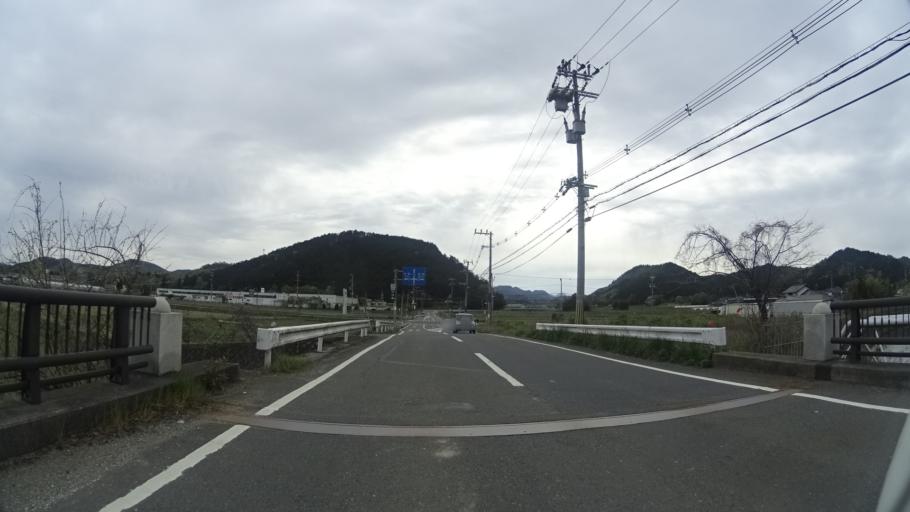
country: JP
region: Kyoto
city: Ayabe
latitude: 35.1839
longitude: 135.4200
